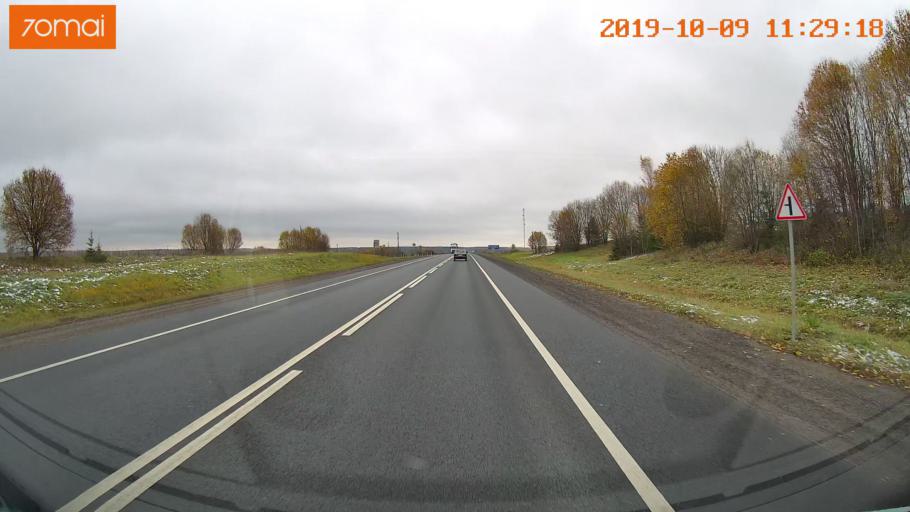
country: RU
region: Vologda
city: Vologda
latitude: 59.0634
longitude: 40.0506
